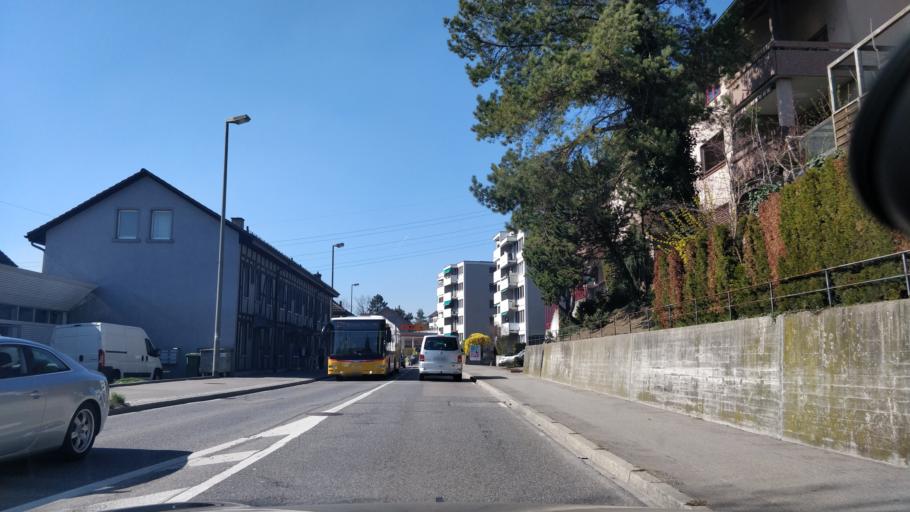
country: CH
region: Zurich
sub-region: Bezirk Winterthur
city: Wuelflingen (Kreis 6) / Haerti
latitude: 47.5155
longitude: 8.6817
